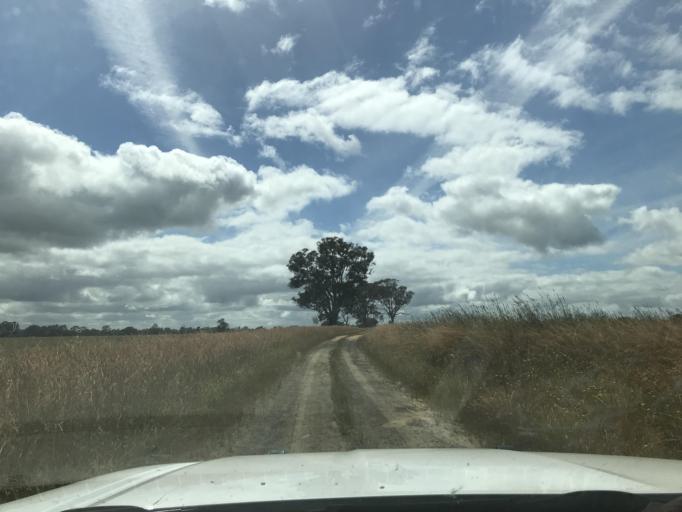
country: AU
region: South Australia
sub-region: Naracoorte and Lucindale
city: Naracoorte
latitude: -37.0089
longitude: 141.0686
